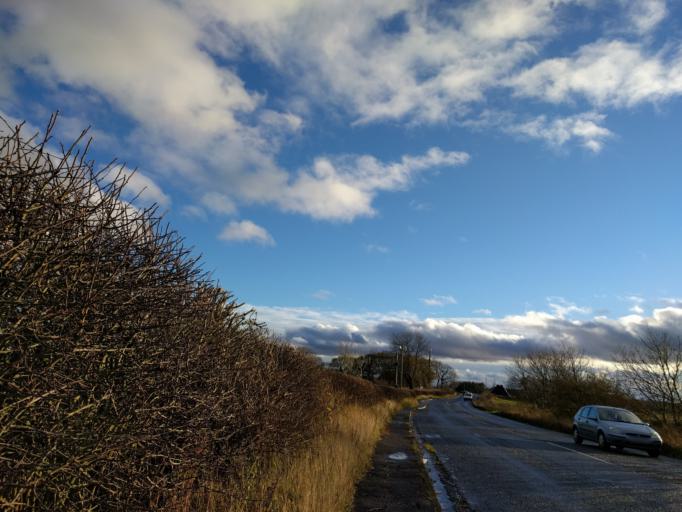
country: GB
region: England
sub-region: Northumberland
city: Cramlington
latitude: 55.1094
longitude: -1.5697
